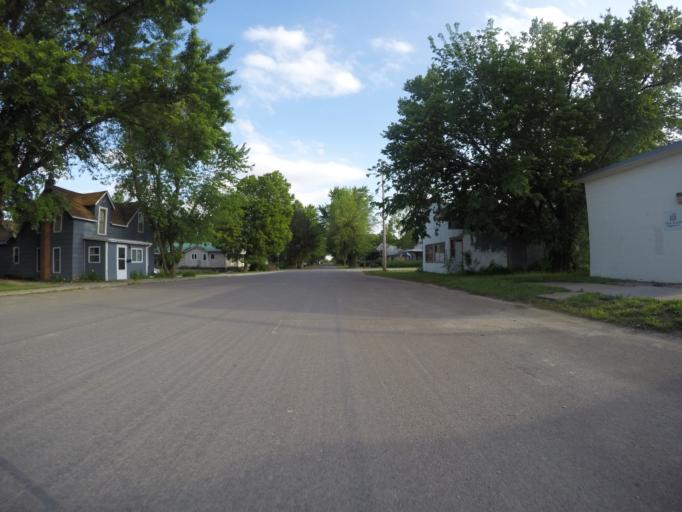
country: US
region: Kansas
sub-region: Pottawatomie County
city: Westmoreland
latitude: 39.4309
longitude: -96.6150
